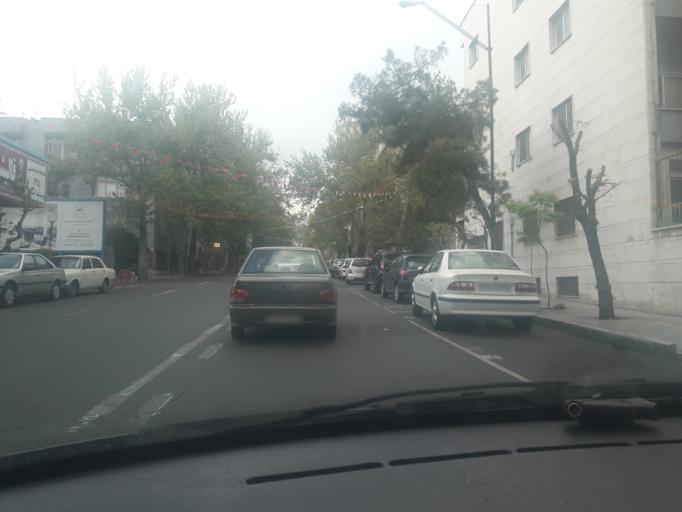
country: IR
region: Tehran
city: Tehran
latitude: 35.7420
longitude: 51.4052
